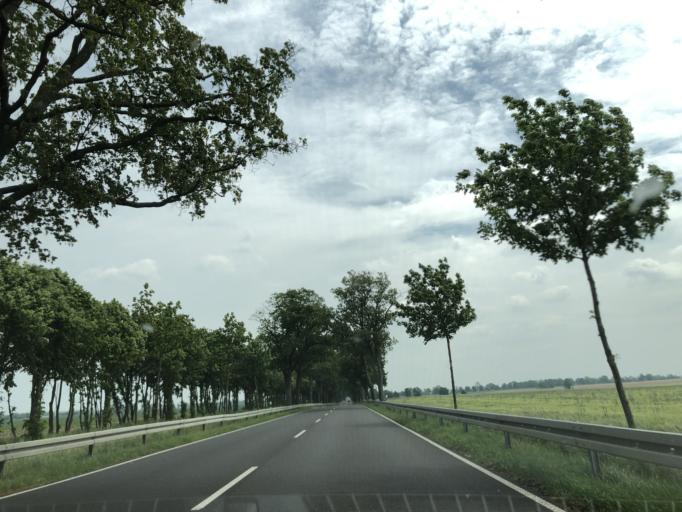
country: DE
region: Brandenburg
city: Gumtow
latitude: 52.9707
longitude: 12.3056
